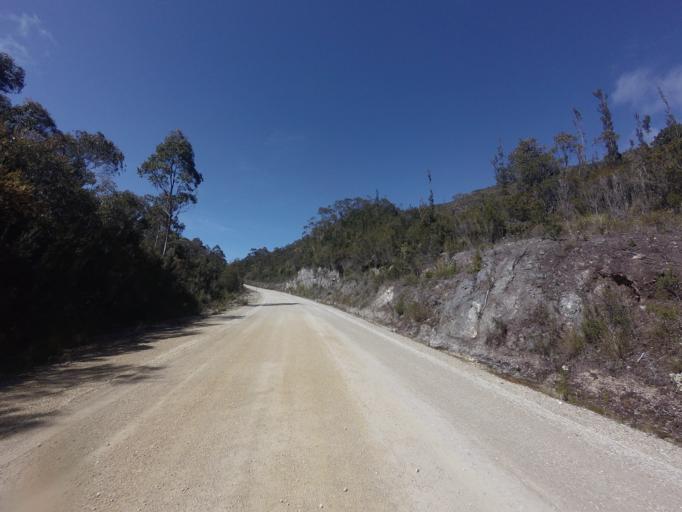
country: AU
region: Tasmania
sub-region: Huon Valley
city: Geeveston
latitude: -42.8160
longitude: 146.3861
